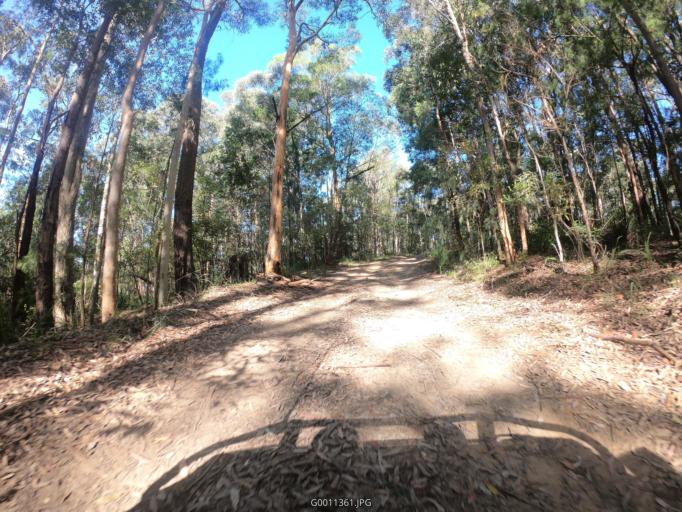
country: AU
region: New South Wales
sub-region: Lake Macquarie Shire
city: Cooranbong
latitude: -33.0249
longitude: 151.3013
